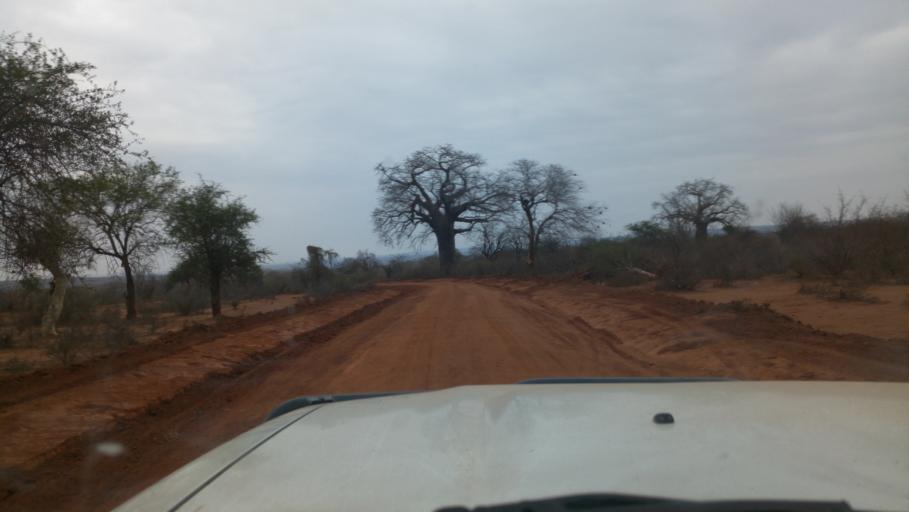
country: KE
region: Makueni
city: Wote
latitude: -1.9170
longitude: 38.1224
